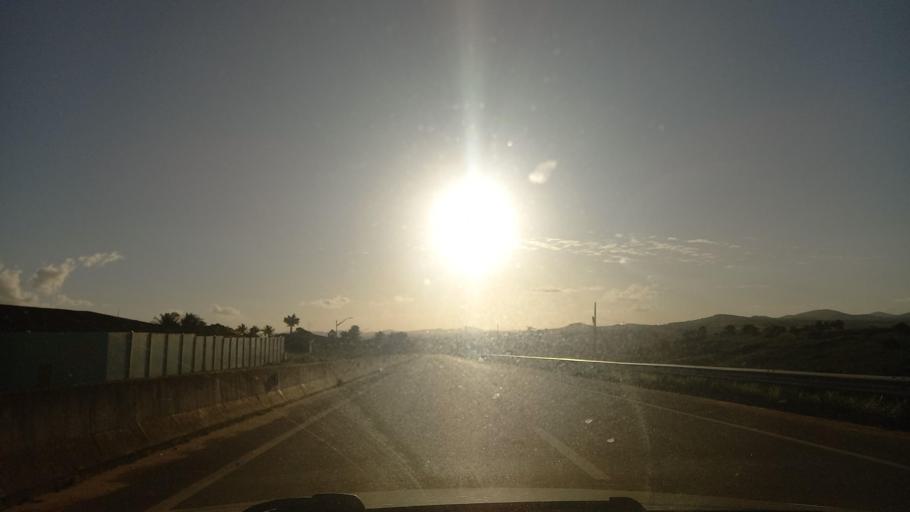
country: BR
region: Alagoas
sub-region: Limoeiro De Anadia
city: Limoeiro de Anadia
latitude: -9.7438
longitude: -36.4743
